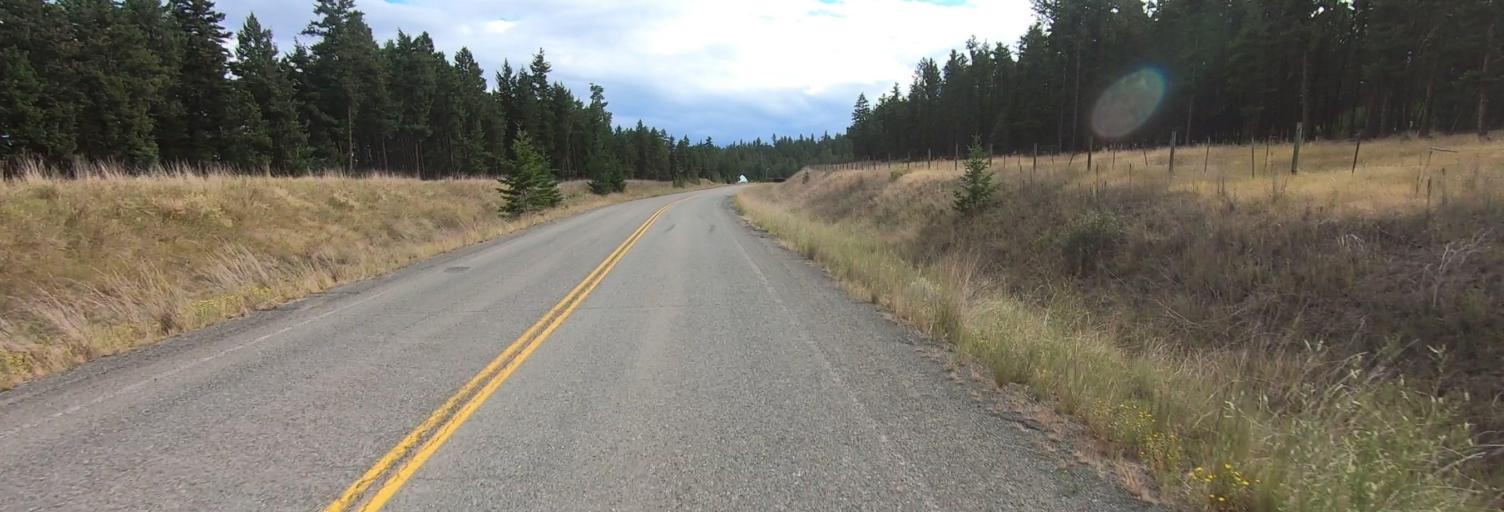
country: CA
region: British Columbia
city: Kamloops
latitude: 50.6193
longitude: -120.4740
